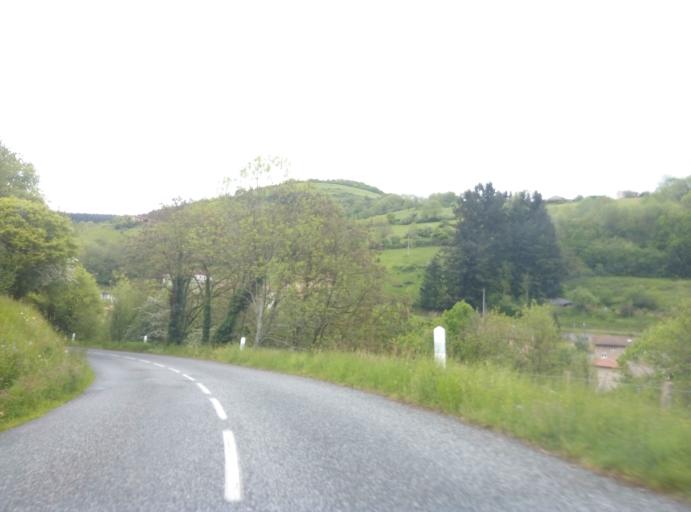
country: FR
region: Rhone-Alpes
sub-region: Departement du Rhone
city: Tarare
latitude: 45.9473
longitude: 4.4258
